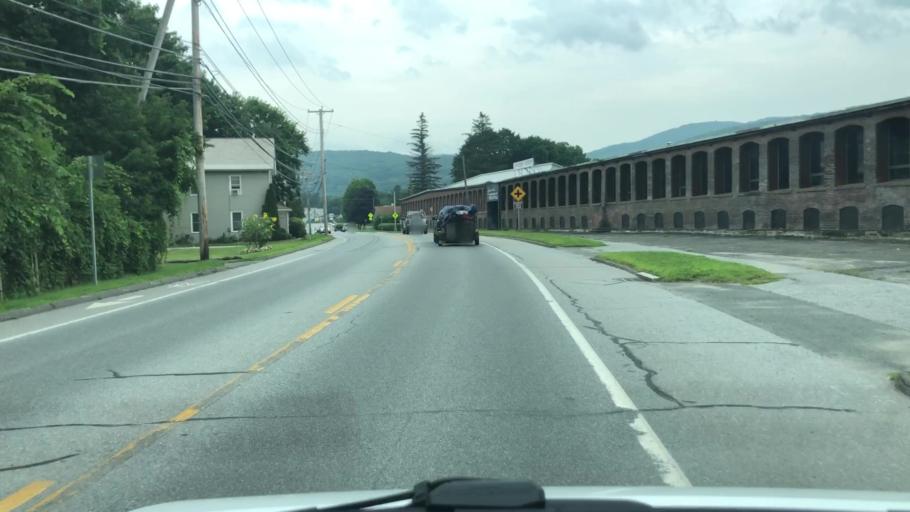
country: US
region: Massachusetts
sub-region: Berkshire County
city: North Adams
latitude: 42.6987
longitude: -73.1524
